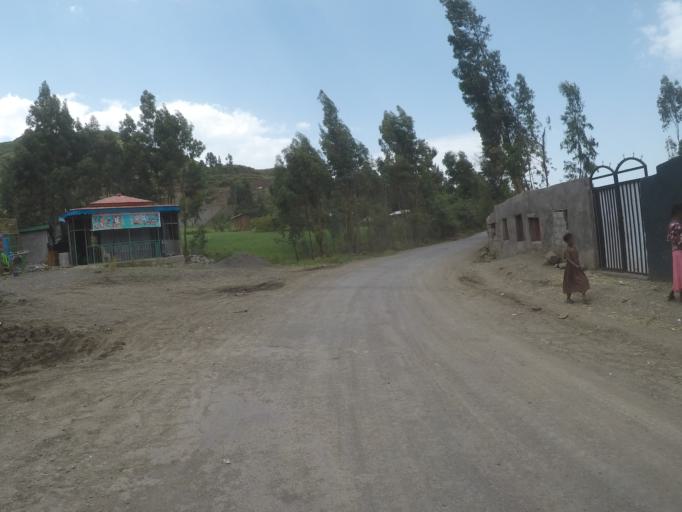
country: ET
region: Amhara
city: Lalibela
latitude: 11.9739
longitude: 38.9959
